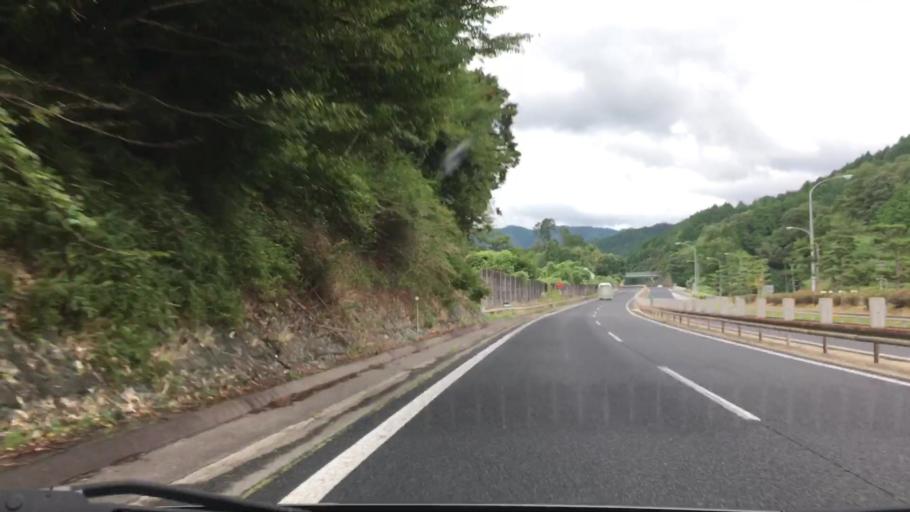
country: JP
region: Okayama
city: Takahashi
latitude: 35.0055
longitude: 133.7285
